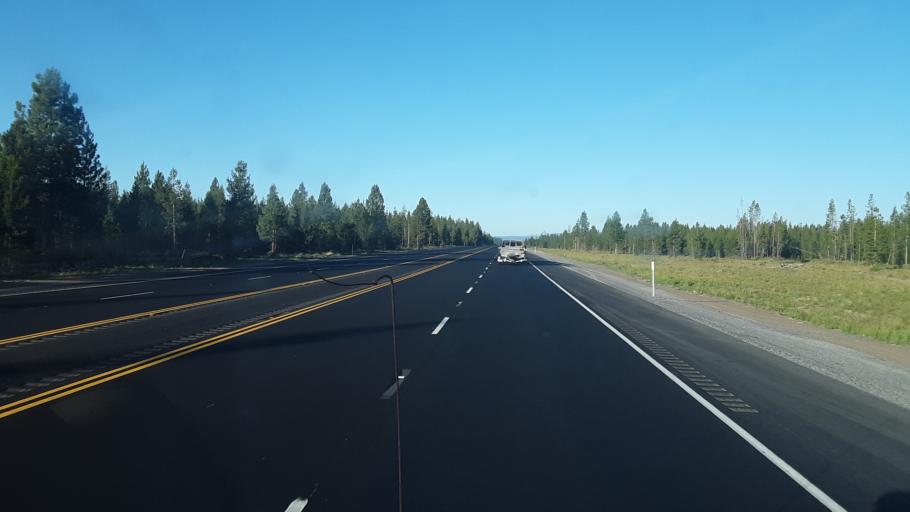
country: US
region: Oregon
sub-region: Deschutes County
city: La Pine
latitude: 43.5211
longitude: -121.6476
